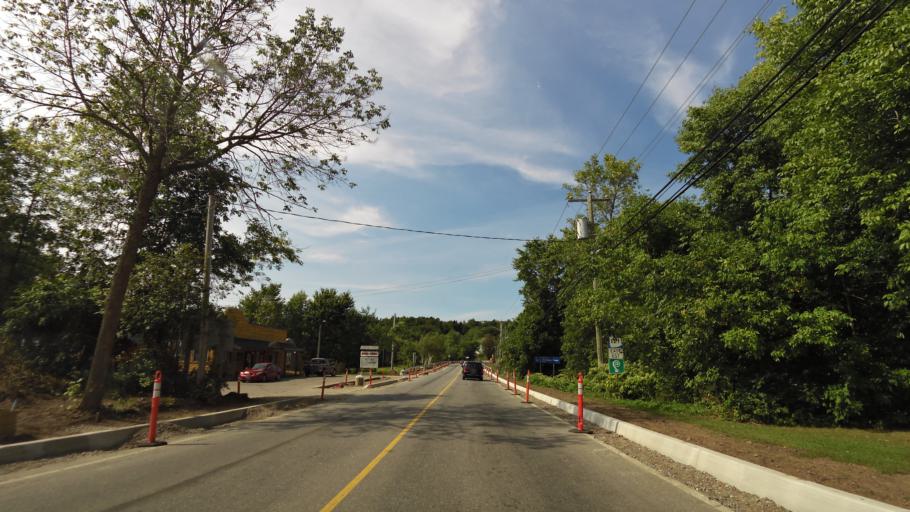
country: CA
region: New Brunswick
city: Hampton
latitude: 45.5264
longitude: -65.8285
